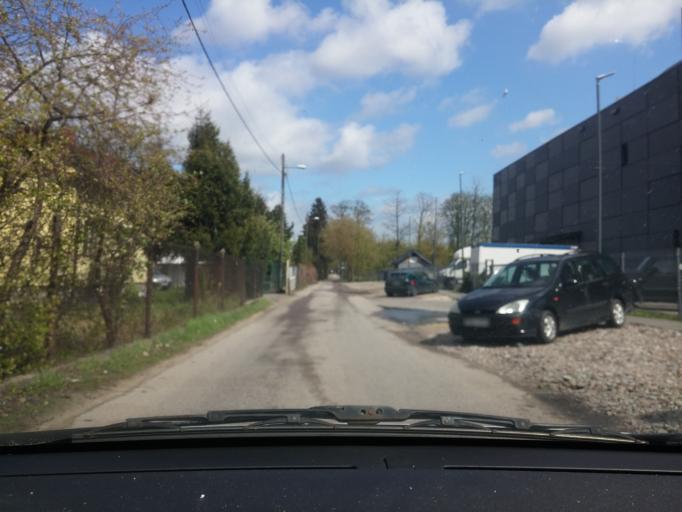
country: PL
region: Masovian Voivodeship
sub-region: Warszawa
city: Wilanow
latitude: 52.1922
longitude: 21.1239
